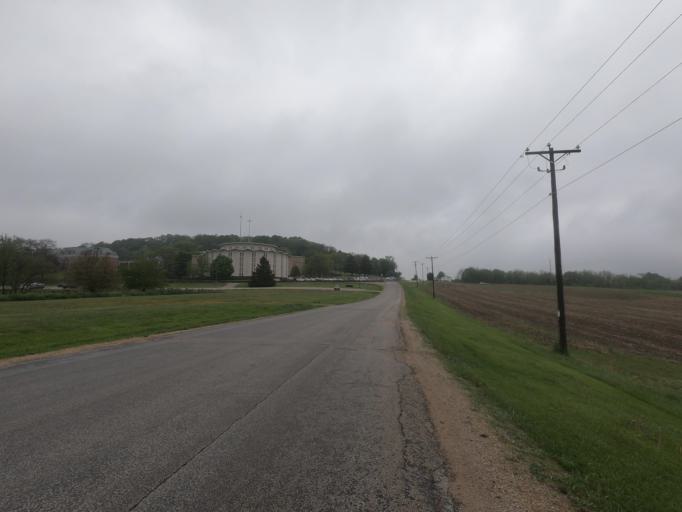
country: US
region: Wisconsin
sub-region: Grant County
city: Hazel Green
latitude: 42.5224
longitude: -90.5391
